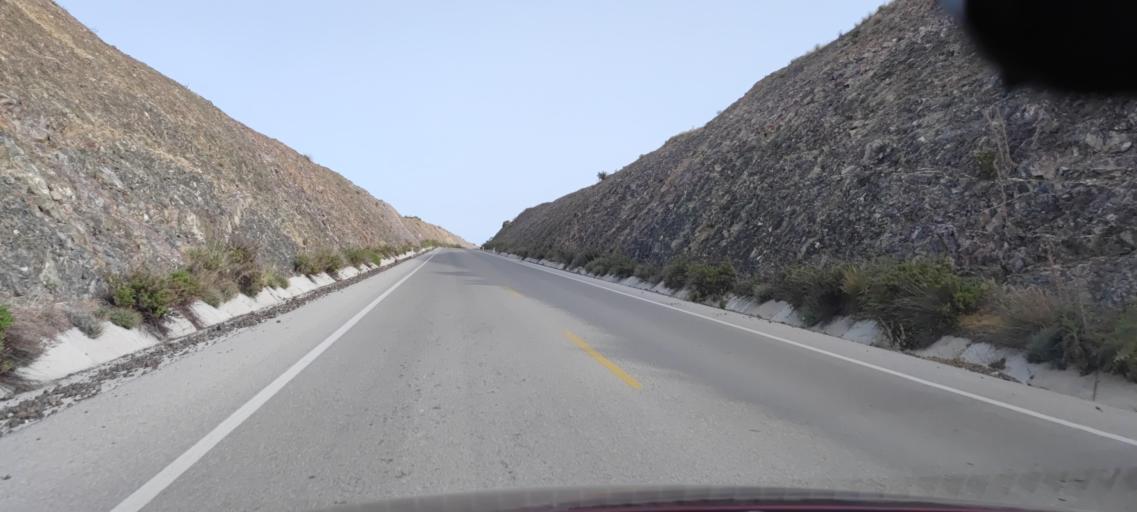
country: CY
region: Ammochostos
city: Leonarisso
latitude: 35.4881
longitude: 34.1007
